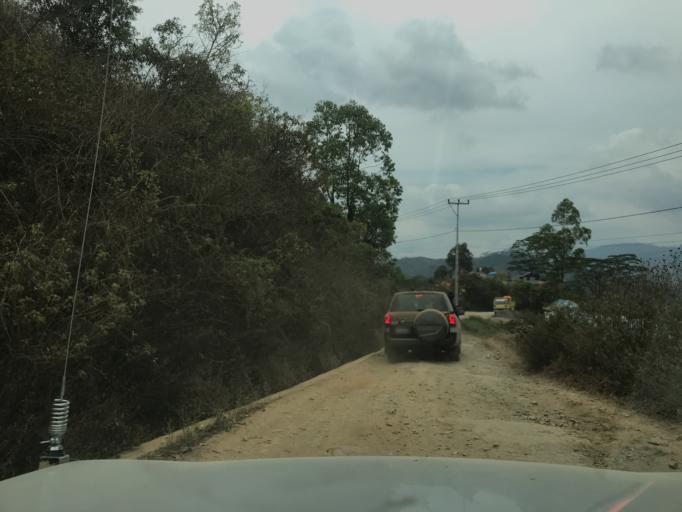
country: TL
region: Ermera
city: Gleno
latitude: -8.8380
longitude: 125.4359
